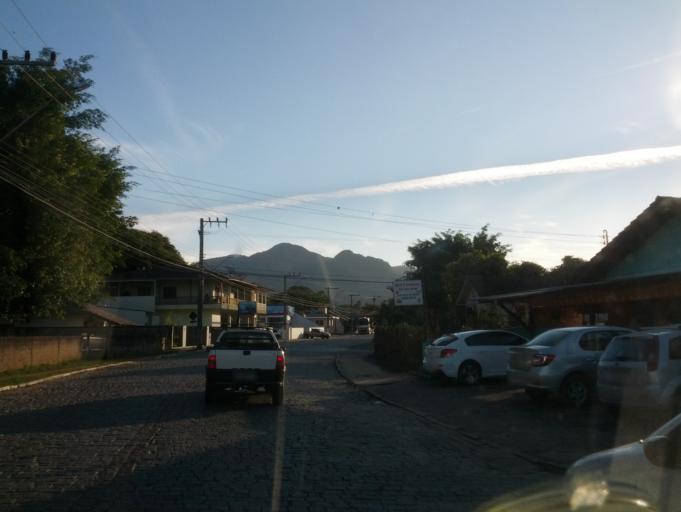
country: BR
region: Santa Catarina
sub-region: Indaial
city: Indaial
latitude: -26.8983
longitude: -49.2499
